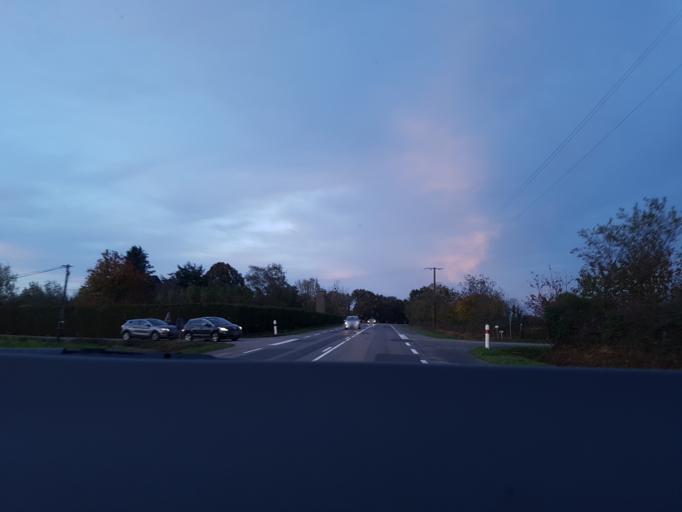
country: FR
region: Pays de la Loire
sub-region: Departement de la Mayenne
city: Cosse-le-Vivien
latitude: 47.9725
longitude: -0.8781
